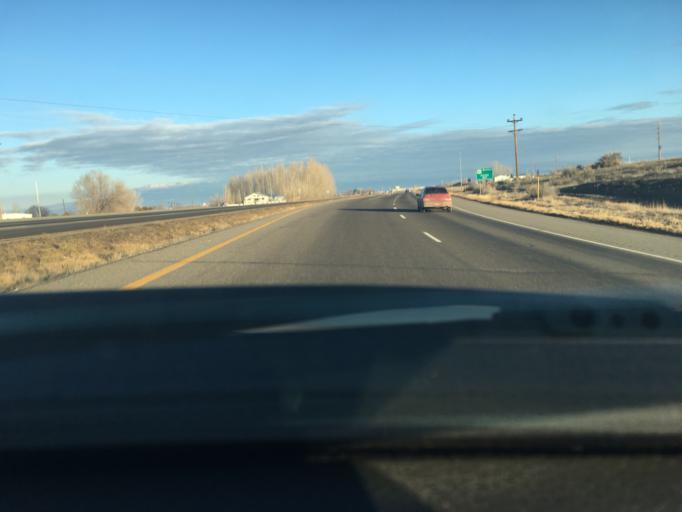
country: US
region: Colorado
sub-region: Montrose County
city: Olathe
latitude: 38.5962
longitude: -107.9728
